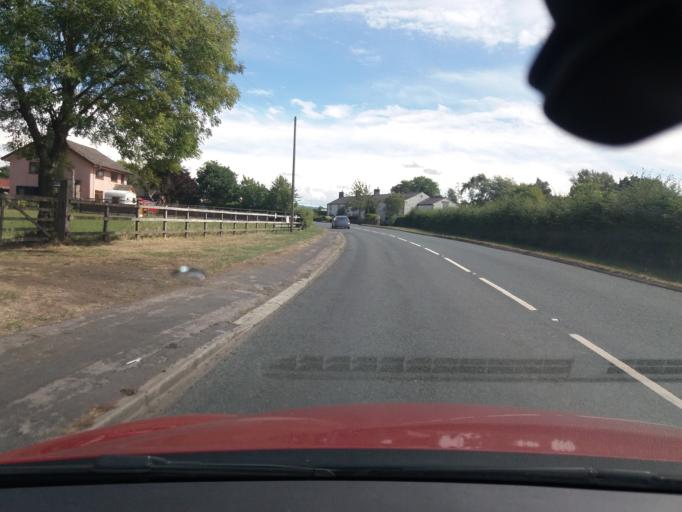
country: GB
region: England
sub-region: Lancashire
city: Euxton
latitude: 53.6605
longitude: -2.7025
